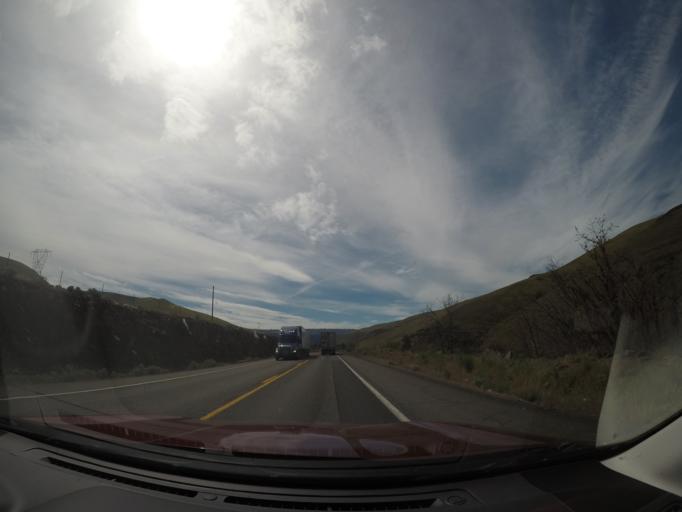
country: US
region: Washington
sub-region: Yakima County
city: Toppenish
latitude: 46.0931
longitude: -120.5481
